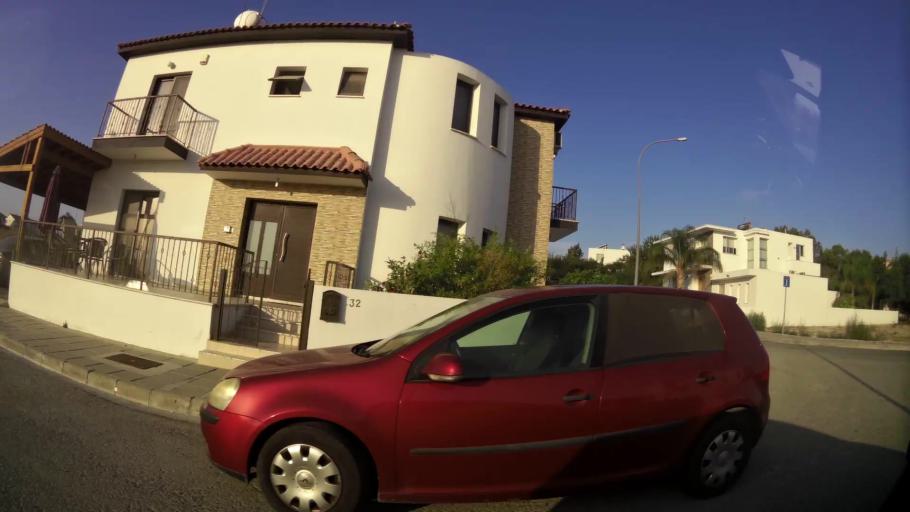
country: CY
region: Larnaka
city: Aradippou
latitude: 34.9266
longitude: 33.5905
